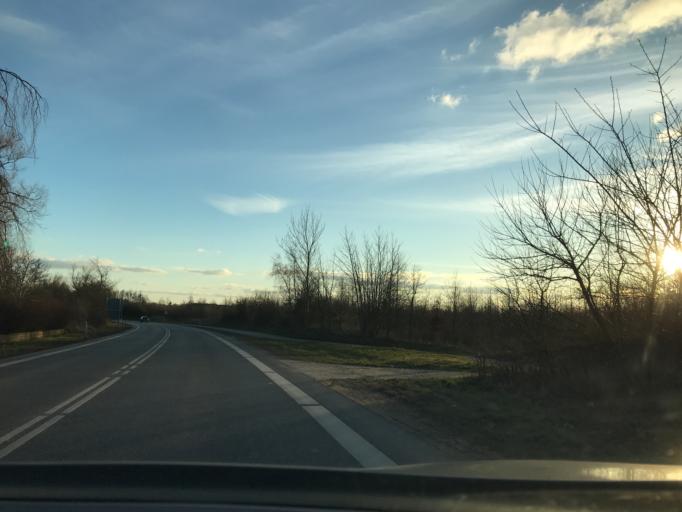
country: DK
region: South Denmark
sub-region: Middelfart Kommune
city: Norre Aby
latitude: 55.4663
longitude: 9.8918
